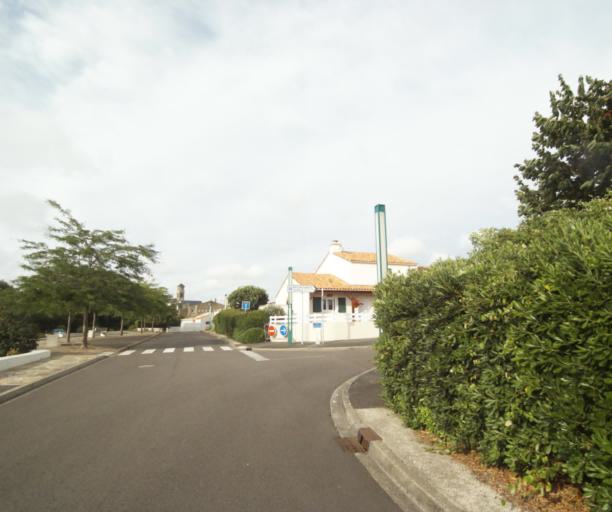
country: FR
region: Pays de la Loire
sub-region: Departement de la Vendee
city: Chateau-d'Olonne
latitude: 46.5034
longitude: -1.7387
